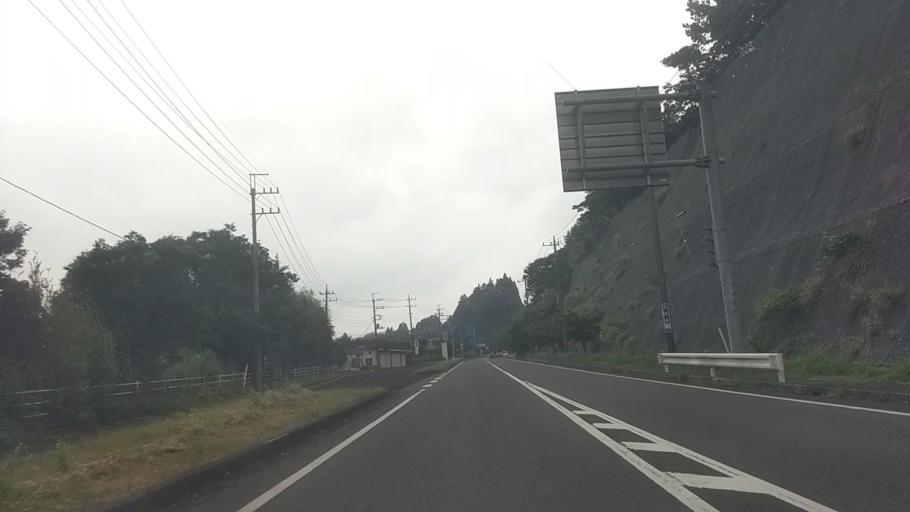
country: JP
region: Chiba
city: Ohara
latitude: 35.2721
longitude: 140.2543
